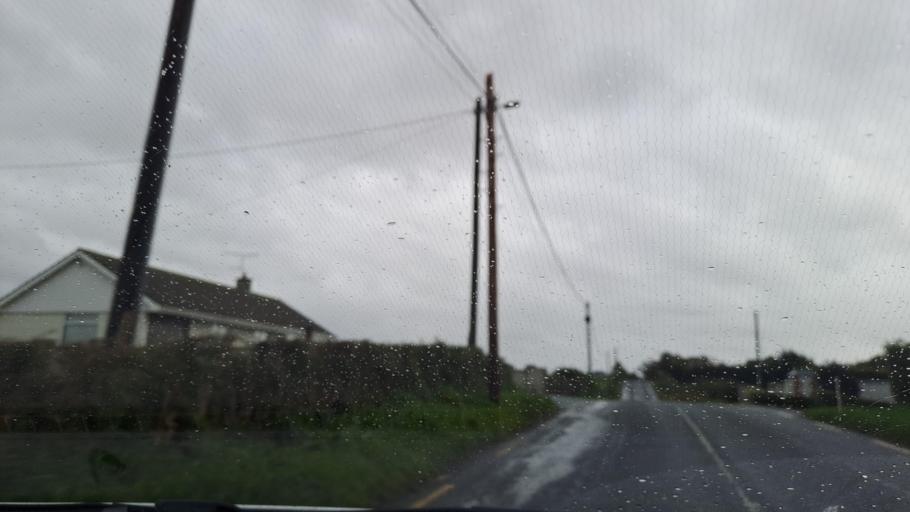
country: IE
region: Leinster
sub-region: Lu
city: Dundalk
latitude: 53.9790
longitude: -6.4923
